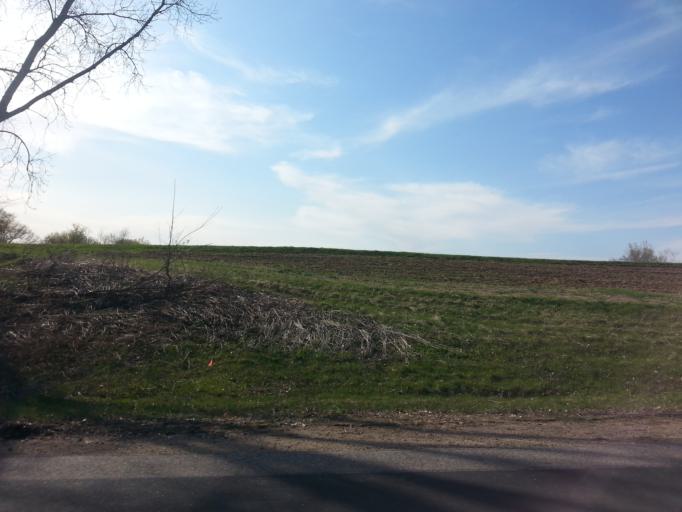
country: US
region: Minnesota
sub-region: Goodhue County
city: Red Wing
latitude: 44.6701
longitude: -92.6054
